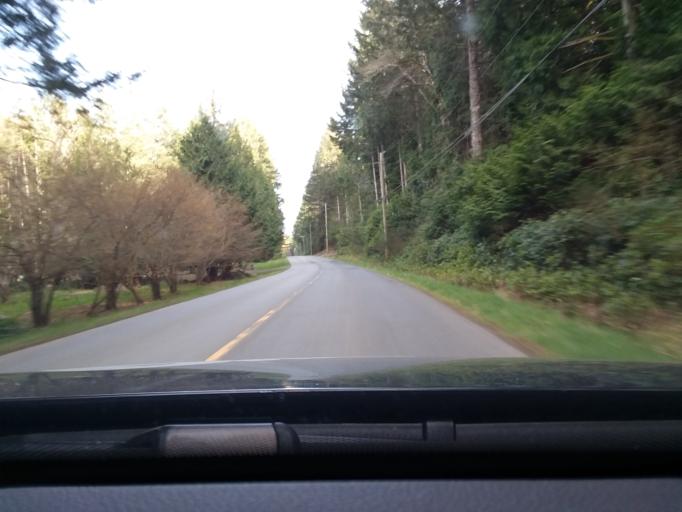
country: CA
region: British Columbia
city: North Saanich
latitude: 48.7509
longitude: -123.2635
